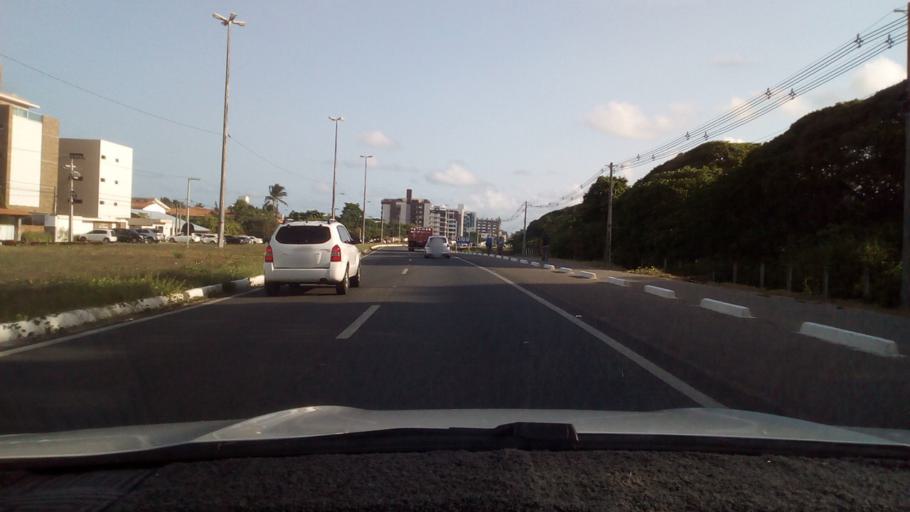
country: BR
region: Paraiba
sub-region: Cabedelo
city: Cabedelo
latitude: -6.9920
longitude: -34.8286
